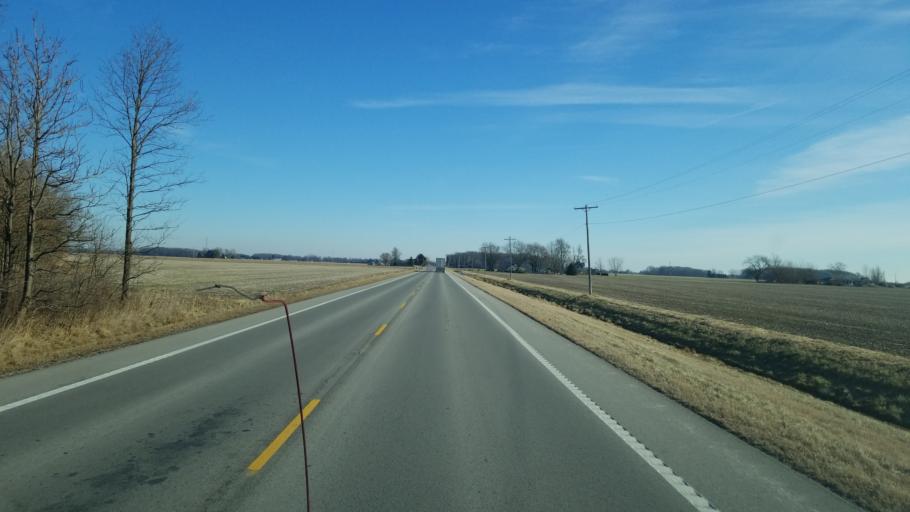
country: US
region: Ohio
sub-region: Henry County
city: Liberty Center
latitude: 41.3712
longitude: -83.9758
